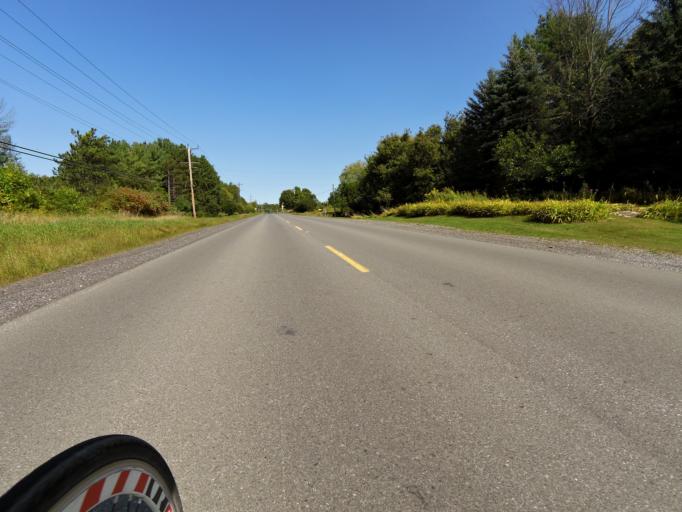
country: CA
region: Ontario
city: Arnprior
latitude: 45.4331
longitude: -76.1214
